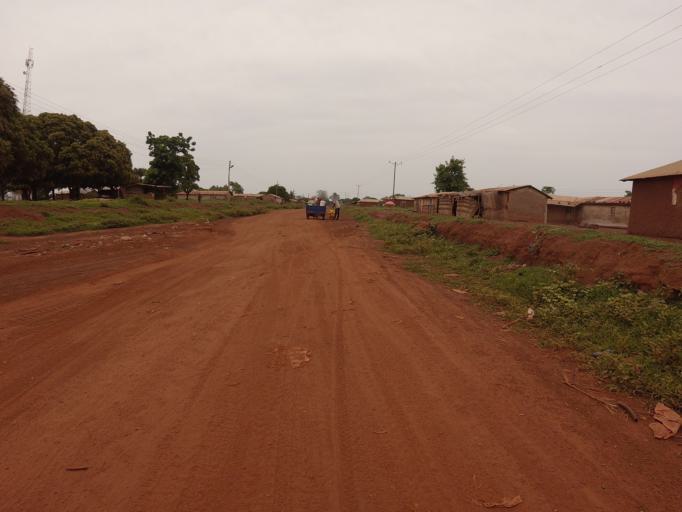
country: GH
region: Northern
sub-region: Yendi
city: Yendi
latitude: 9.2152
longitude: 0.0213
